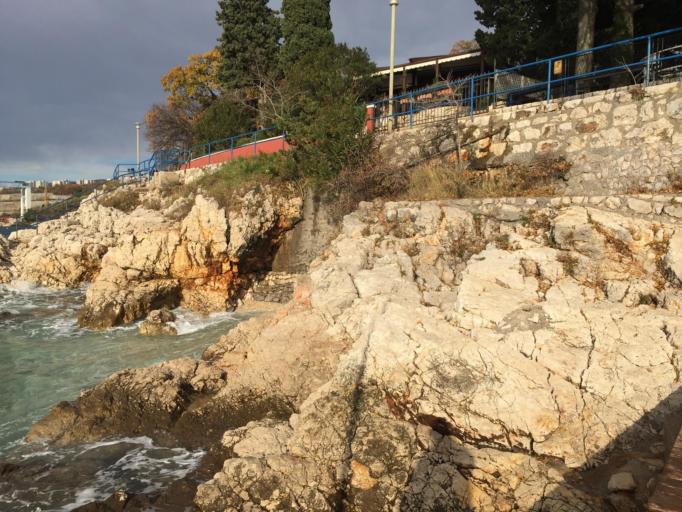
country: HR
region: Primorsko-Goranska
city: Skrljevo
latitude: 45.3028
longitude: 14.4882
